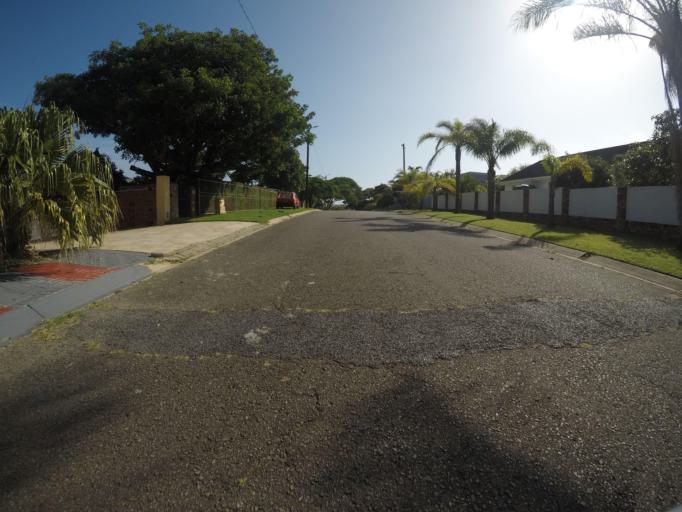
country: ZA
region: Eastern Cape
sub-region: Buffalo City Metropolitan Municipality
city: East London
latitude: -32.9747
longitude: 27.9562
